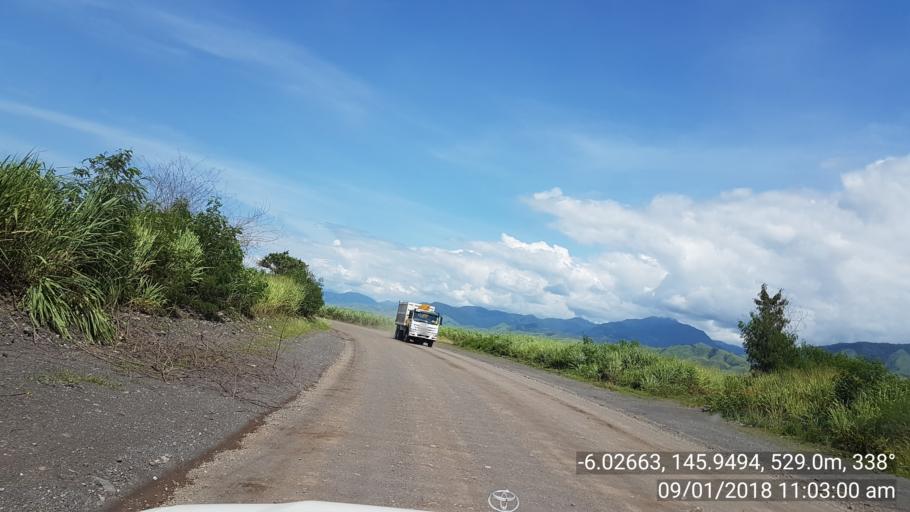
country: PG
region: Eastern Highlands
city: Kainantu
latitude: -6.0268
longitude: 145.9494
